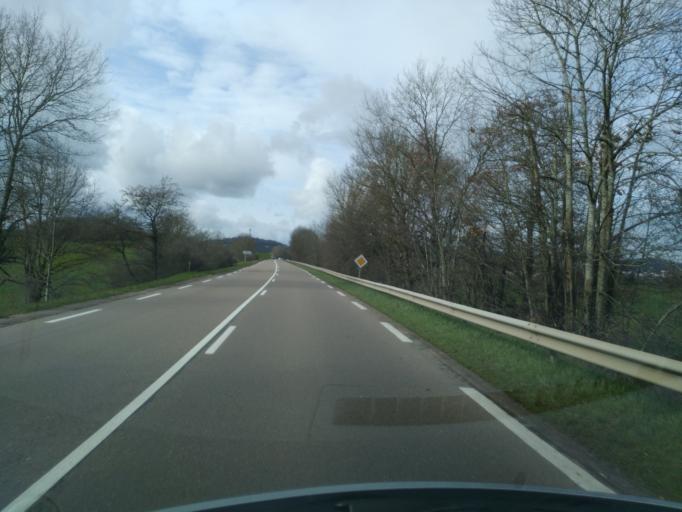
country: FR
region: Bourgogne
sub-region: Departement de Saone-et-Loire
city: Torcy
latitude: 46.7734
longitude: 4.4274
